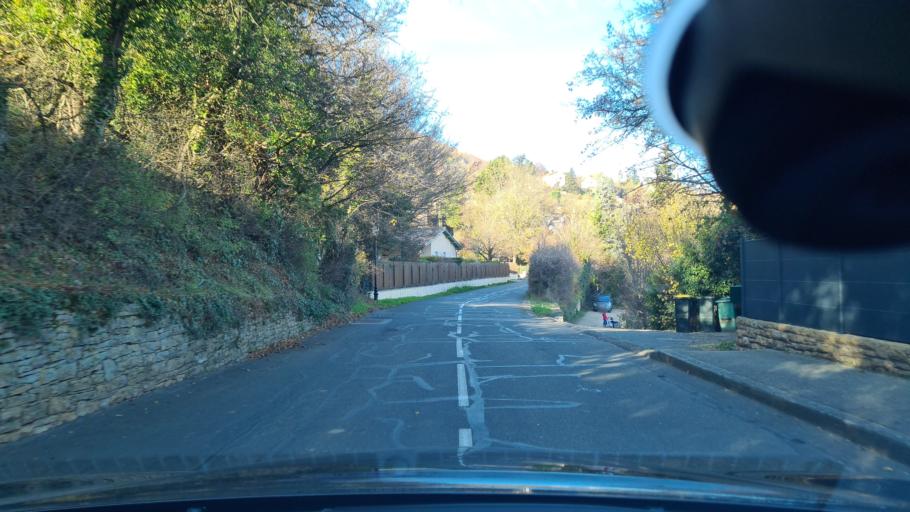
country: FR
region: Rhone-Alpes
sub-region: Departement du Rhone
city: Chasselay
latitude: 45.8568
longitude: 4.7965
